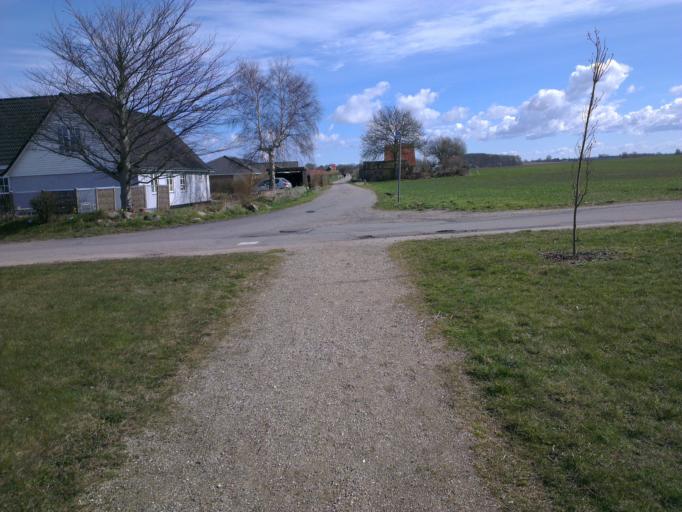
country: DK
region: Capital Region
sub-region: Frederikssund Kommune
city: Frederikssund
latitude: 55.8166
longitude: 12.0762
